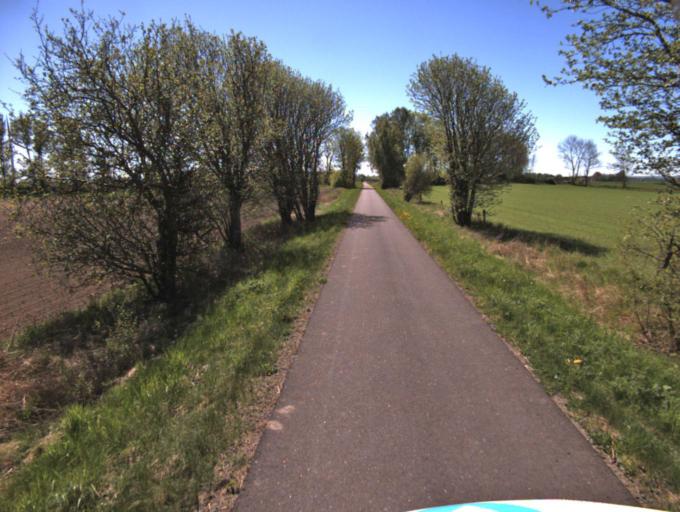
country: SE
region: Skane
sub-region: Kristianstads Kommun
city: Norra Asum
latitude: 55.9627
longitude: 14.1578
